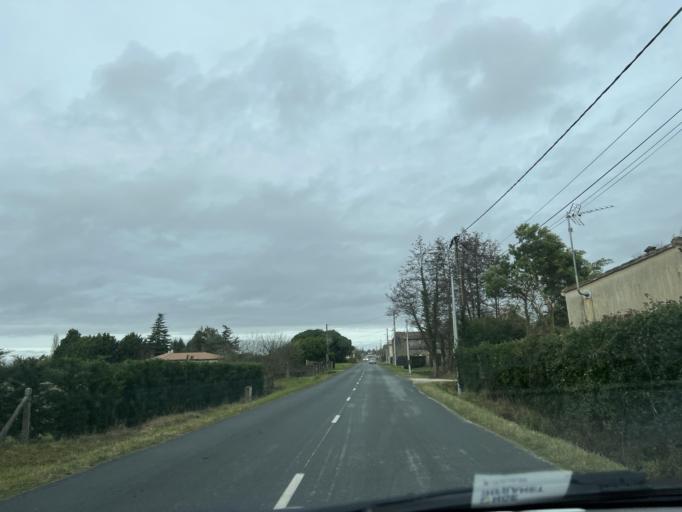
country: FR
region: Aquitaine
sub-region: Departement de la Gironde
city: Saint-Ciers-sur-Gironde
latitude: 45.2773
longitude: -0.6146
